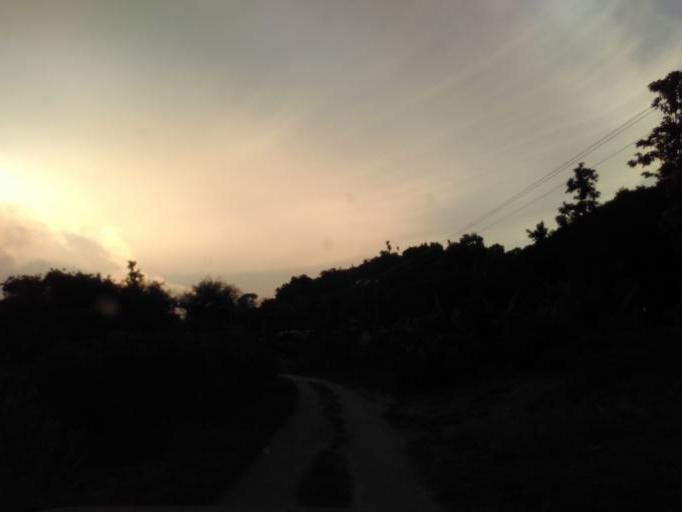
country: GH
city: Bekwai
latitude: 6.5237
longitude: -1.4394
